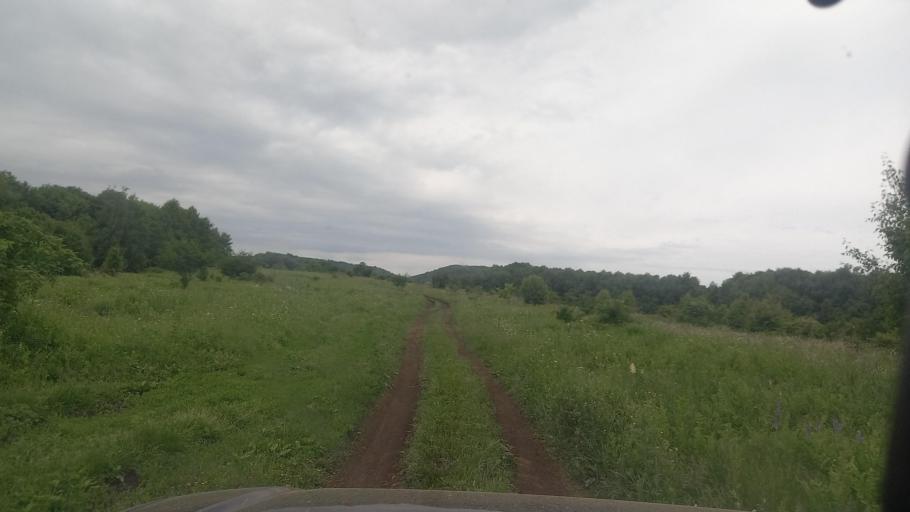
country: RU
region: Karachayevo-Cherkesiya
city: Pregradnaya
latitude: 44.0332
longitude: 41.3120
